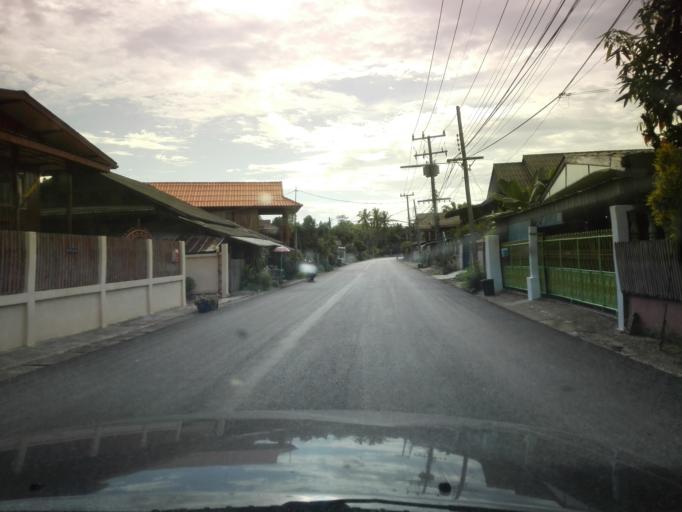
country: TH
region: Tak
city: Mae Ramat
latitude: 16.9821
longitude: 98.5155
